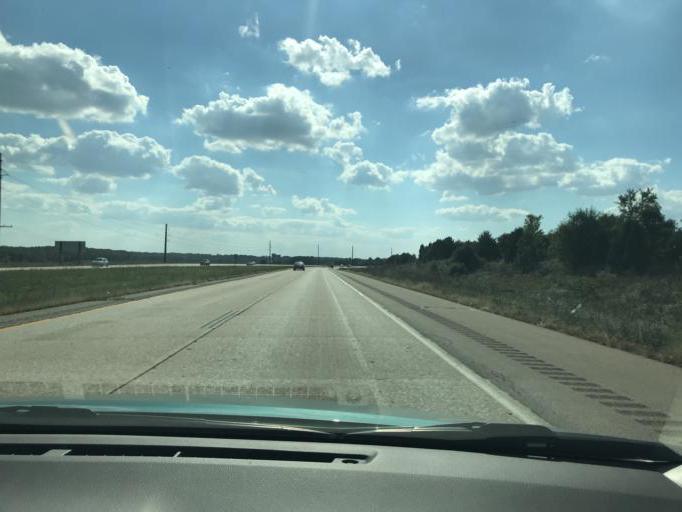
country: US
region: Wisconsin
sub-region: Walworth County
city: Delavan
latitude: 42.6163
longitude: -88.6347
